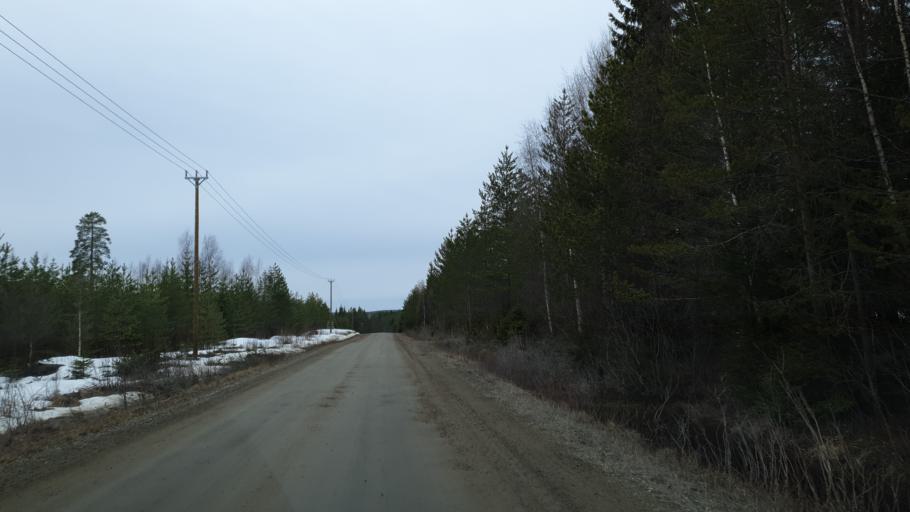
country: SE
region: Vaesterbotten
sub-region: Robertsfors Kommun
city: Robertsfors
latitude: 64.3890
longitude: 20.9596
